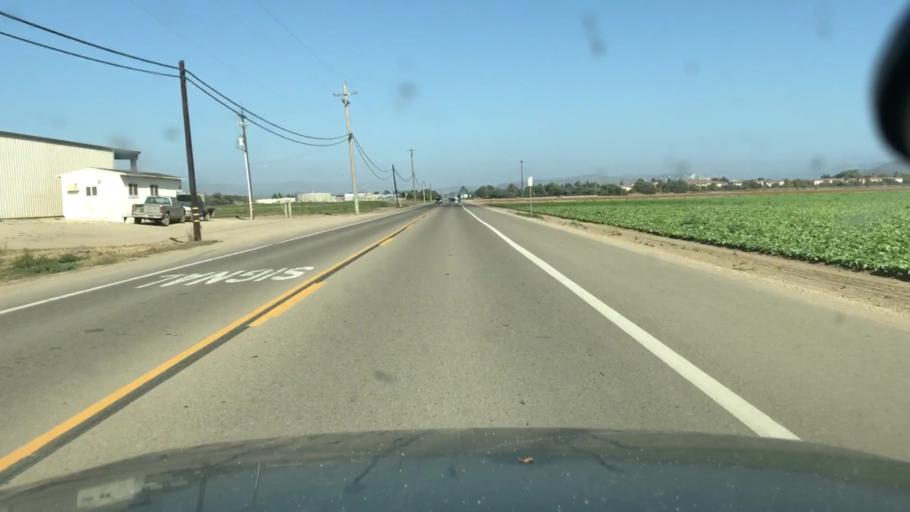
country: US
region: California
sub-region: Santa Barbara County
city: Lompoc
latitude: 34.6612
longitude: -120.4909
